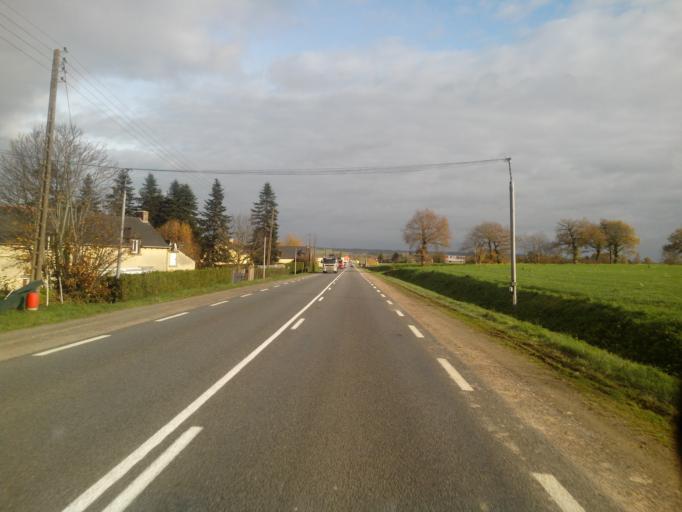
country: FR
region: Brittany
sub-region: Departement d'Ille-et-Vilaine
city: Boisgervilly
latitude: 48.1945
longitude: -2.1100
